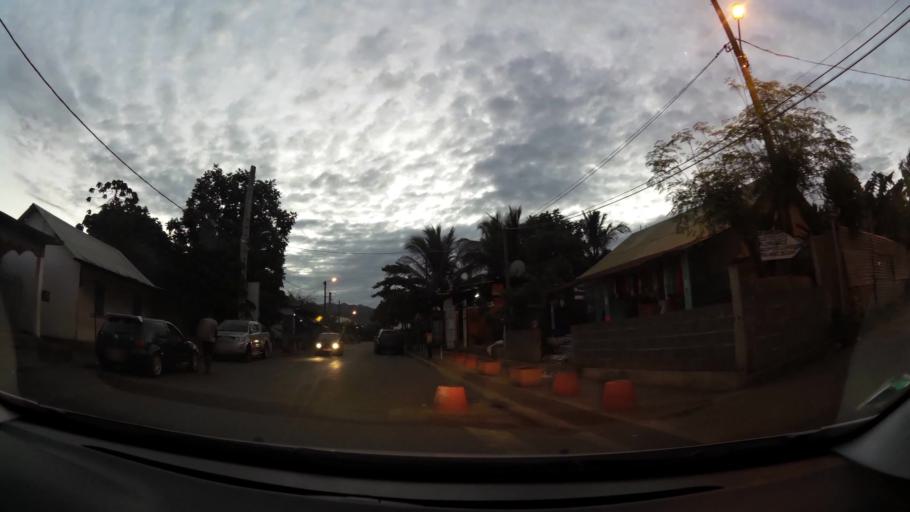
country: YT
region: Bandraboua
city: Bandraboua
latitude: -12.7226
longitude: 45.1194
